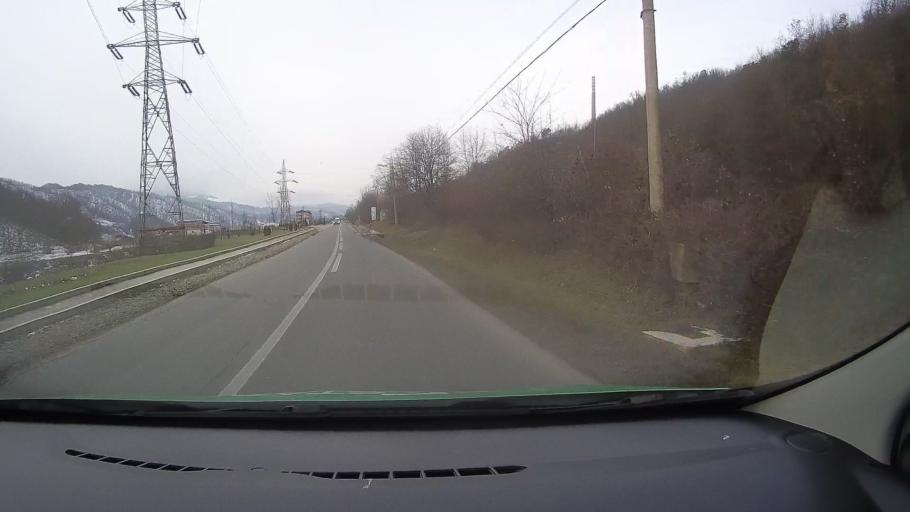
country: RO
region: Alba
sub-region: Oras Zlatna
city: Zlatna
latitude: 46.1048
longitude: 23.2442
